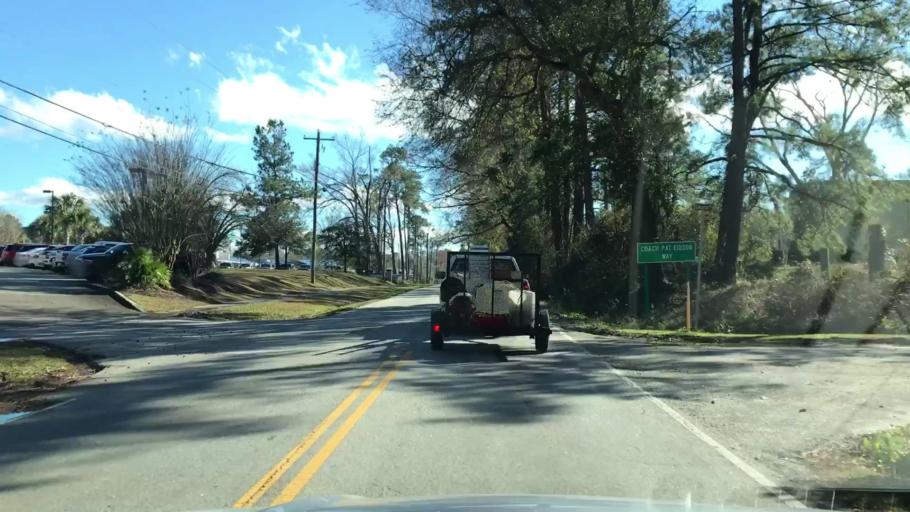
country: US
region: South Carolina
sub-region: Dorchester County
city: Summerville
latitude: 33.0254
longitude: -80.2430
